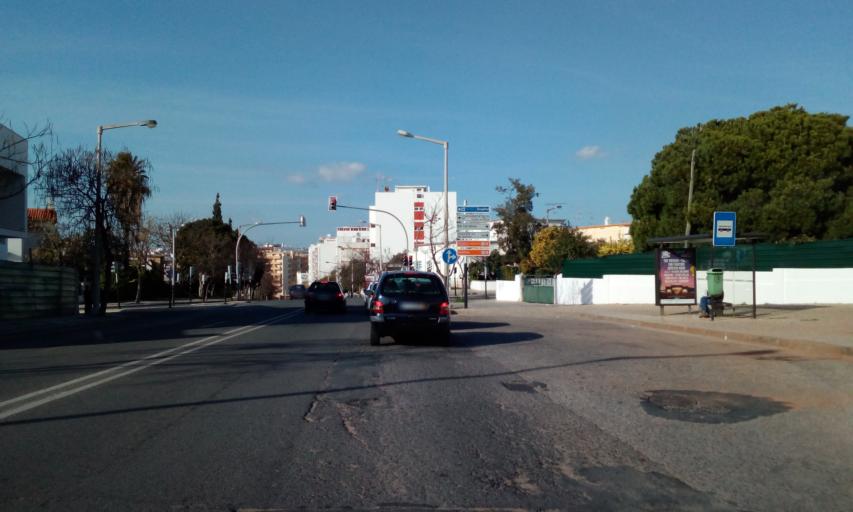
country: PT
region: Faro
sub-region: Faro
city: Faro
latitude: 37.0206
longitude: -7.9235
